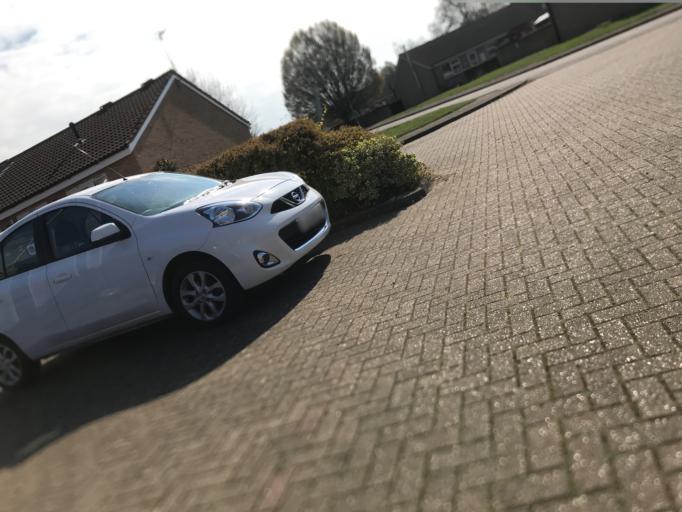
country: GB
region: England
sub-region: Cambridgeshire
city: Sawston
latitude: 52.1520
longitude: 0.1393
